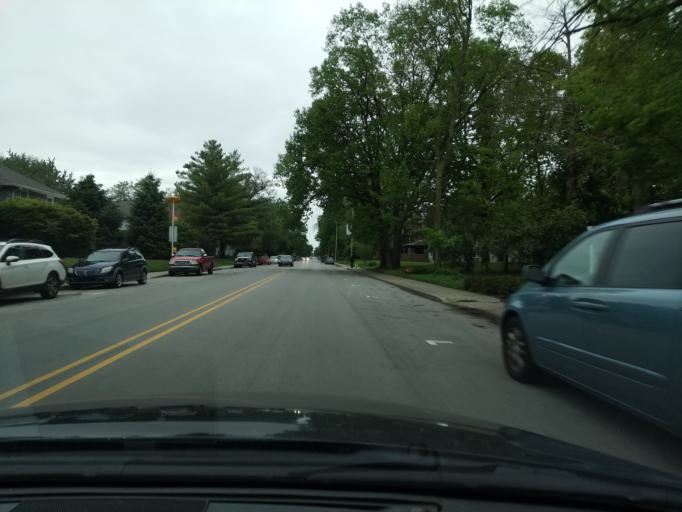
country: US
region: Indiana
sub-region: Marion County
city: Broad Ripple
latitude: 39.8311
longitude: -86.1498
